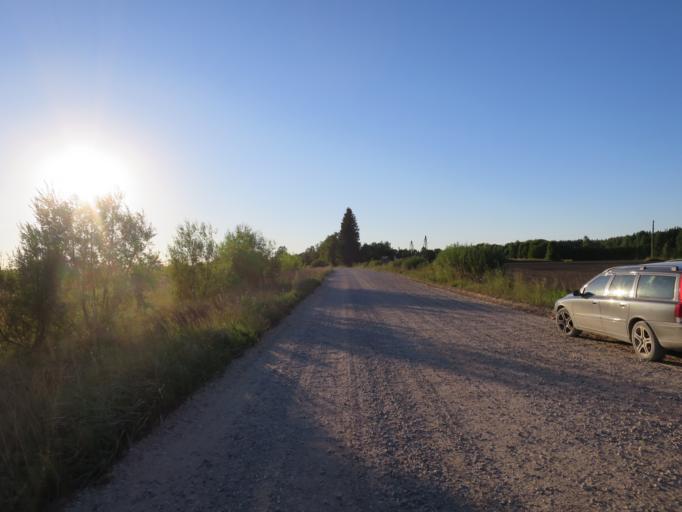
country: LV
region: Malpils
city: Malpils
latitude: 57.1015
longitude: 24.9934
